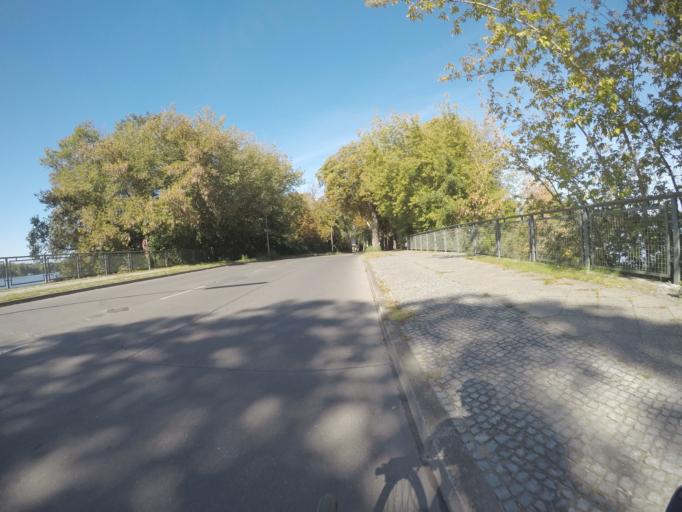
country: DE
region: Berlin
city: Konradshohe
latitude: 52.6016
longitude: 13.2104
